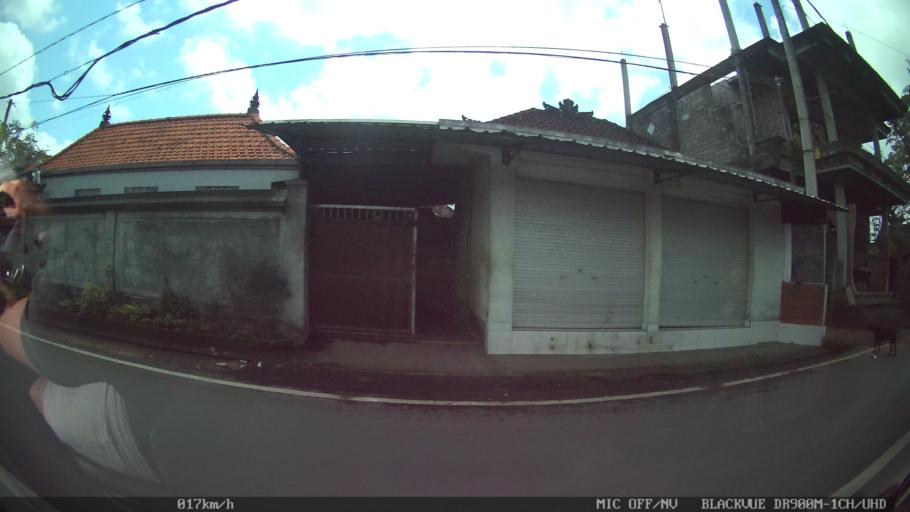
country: ID
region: Bali
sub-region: Kabupaten Gianyar
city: Ubud
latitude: -8.5453
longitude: 115.2803
